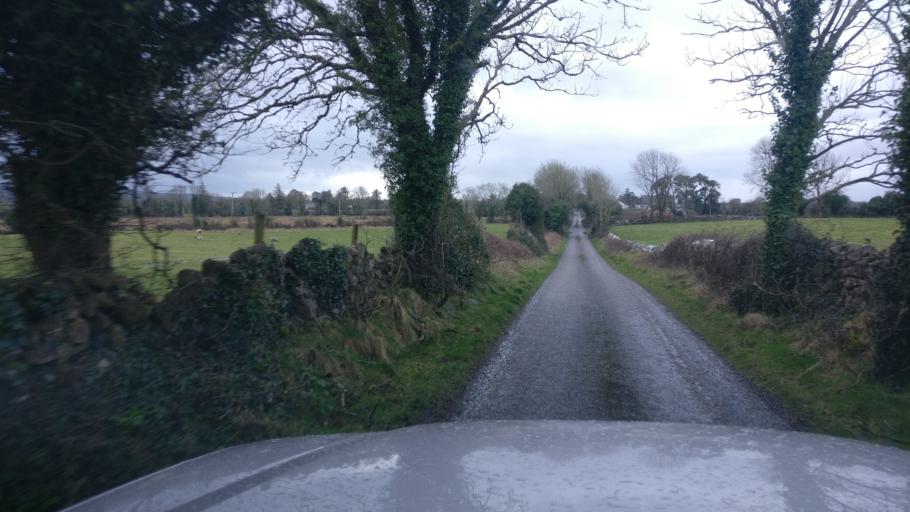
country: IE
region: Connaught
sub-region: County Galway
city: Athenry
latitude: 53.1929
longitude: -8.6876
